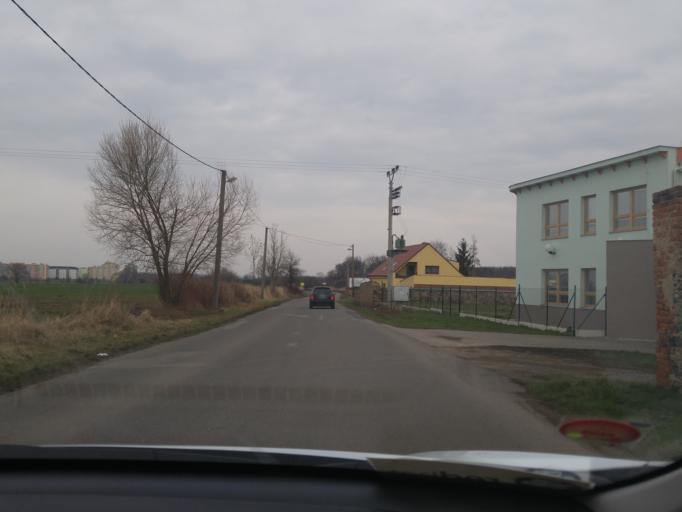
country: CZ
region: Central Bohemia
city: Neratovice
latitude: 50.2401
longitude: 14.5072
